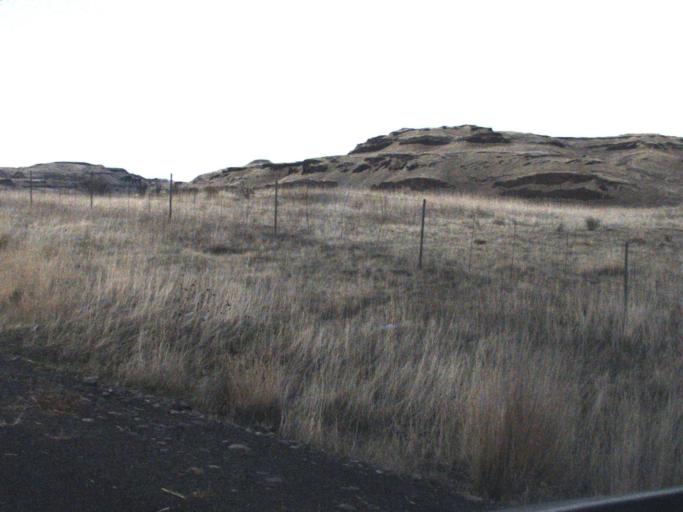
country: US
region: Washington
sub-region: Walla Walla County
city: Waitsburg
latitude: 46.5759
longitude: -118.2080
